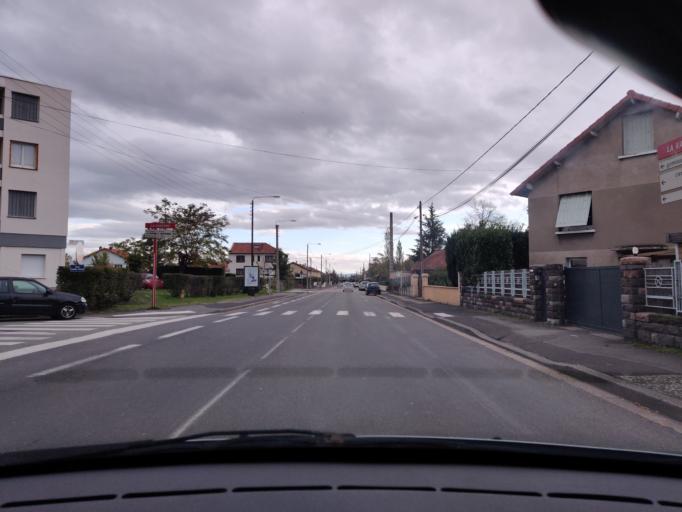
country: FR
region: Auvergne
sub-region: Departement du Puy-de-Dome
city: Menetrol
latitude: 45.8841
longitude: 3.1235
